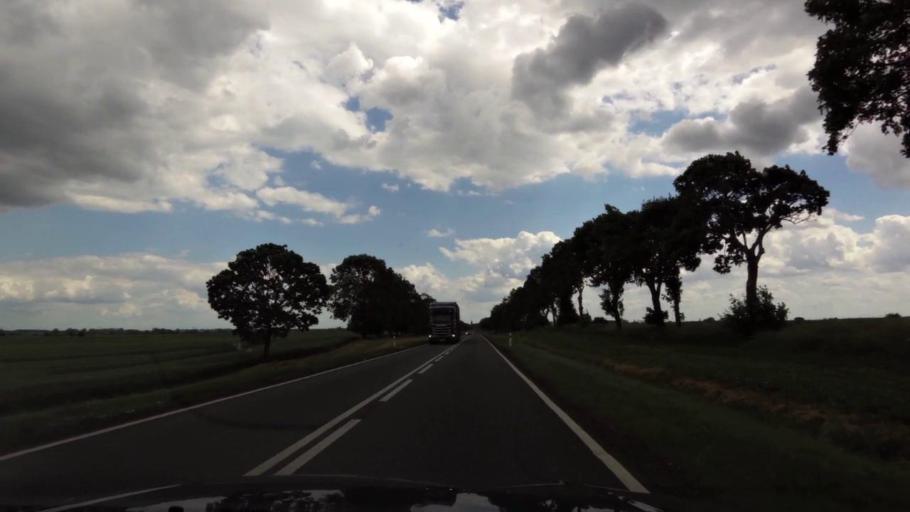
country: PL
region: West Pomeranian Voivodeship
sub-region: Powiat mysliborski
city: Mysliborz
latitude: 52.9609
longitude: 14.7593
